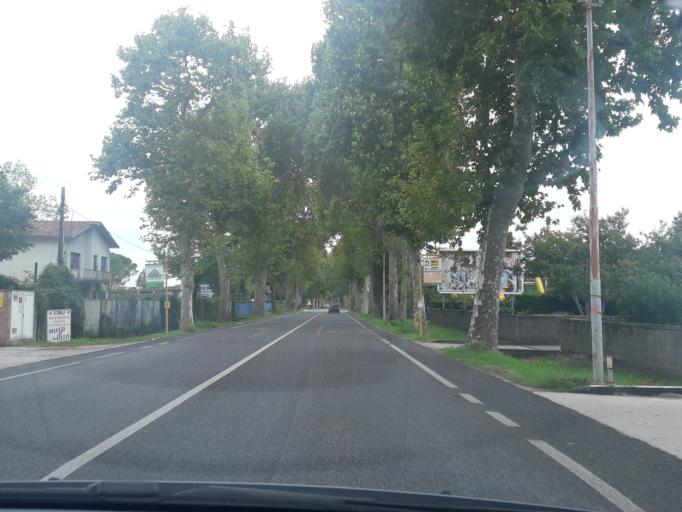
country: IT
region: Friuli Venezia Giulia
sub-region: Provincia di Udine
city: Udine
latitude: 46.0432
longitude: 13.2516
